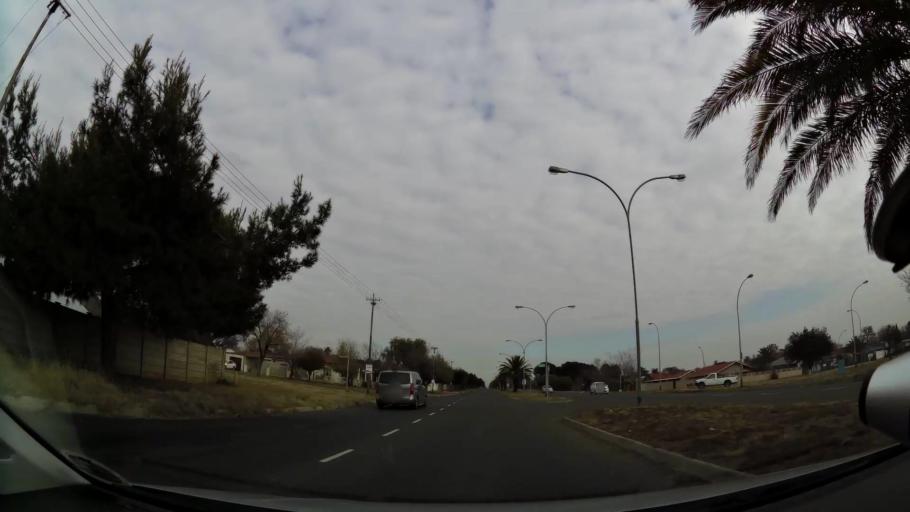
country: ZA
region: Orange Free State
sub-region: Mangaung Metropolitan Municipality
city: Bloemfontein
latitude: -29.1262
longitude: 26.1844
